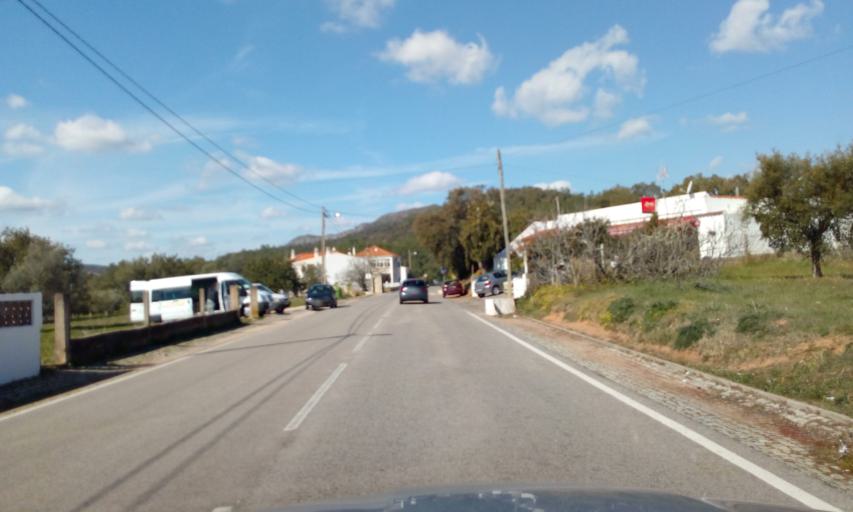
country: PT
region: Faro
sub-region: Loule
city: Loule
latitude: 37.2451
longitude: -8.0661
